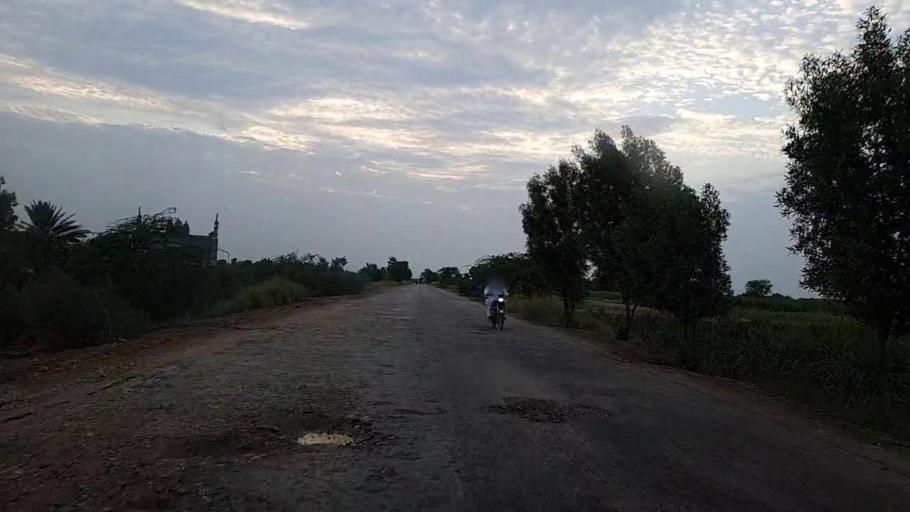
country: PK
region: Sindh
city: Naushahro Firoz
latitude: 26.8199
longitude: 68.1703
